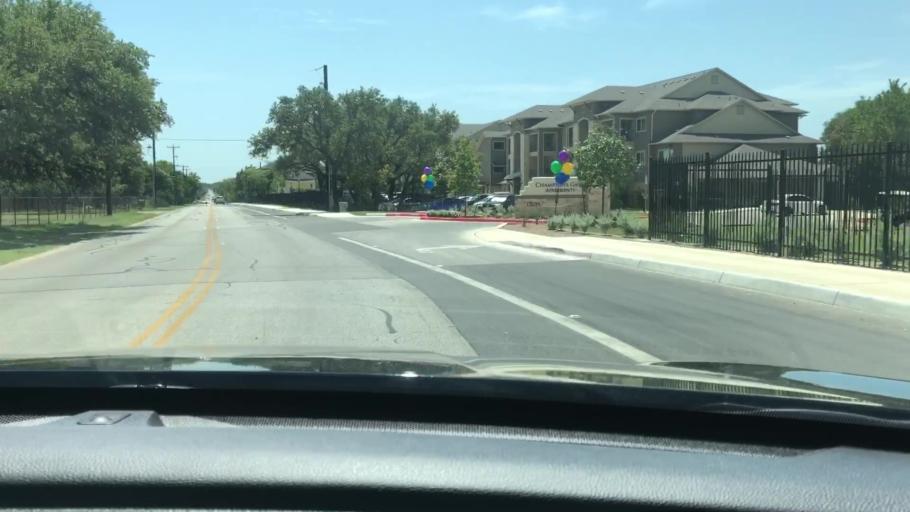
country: US
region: Texas
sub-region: Bexar County
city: Helotes
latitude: 29.5616
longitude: -98.6558
